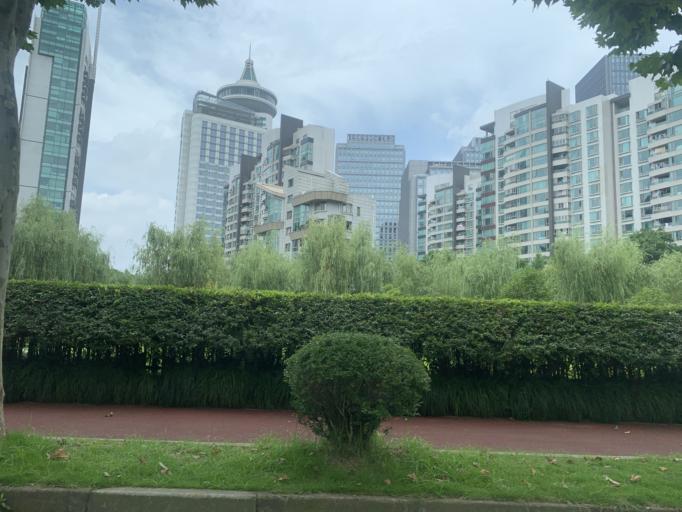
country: CN
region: Shanghai Shi
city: Huamu
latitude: 31.2131
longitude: 121.5337
